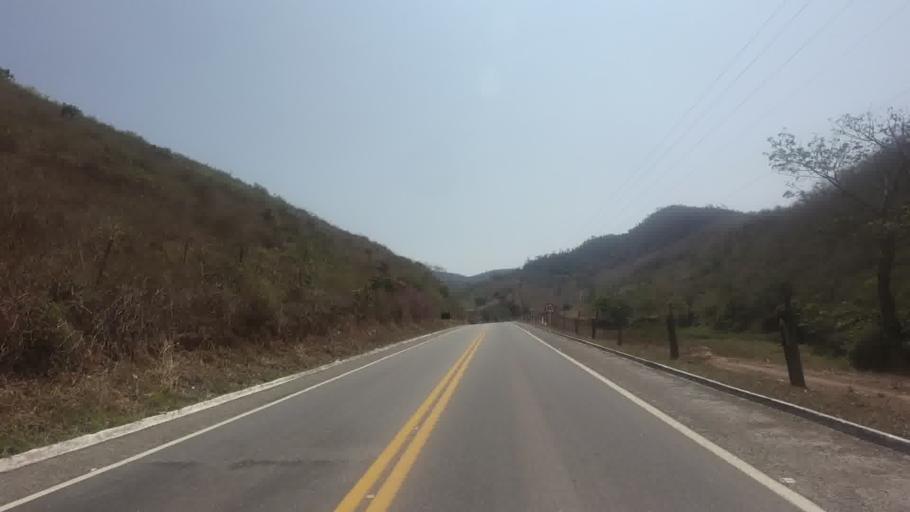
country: BR
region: Espirito Santo
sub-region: Cachoeiro De Itapemirim
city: Cachoeiro de Itapemirim
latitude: -20.8251
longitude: -41.1945
